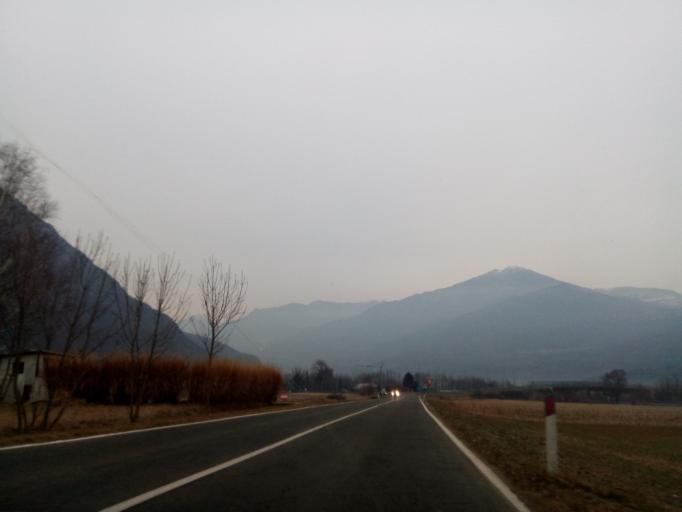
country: IT
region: Piedmont
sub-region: Provincia di Torino
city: Lessolo
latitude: 45.4976
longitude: 7.8284
